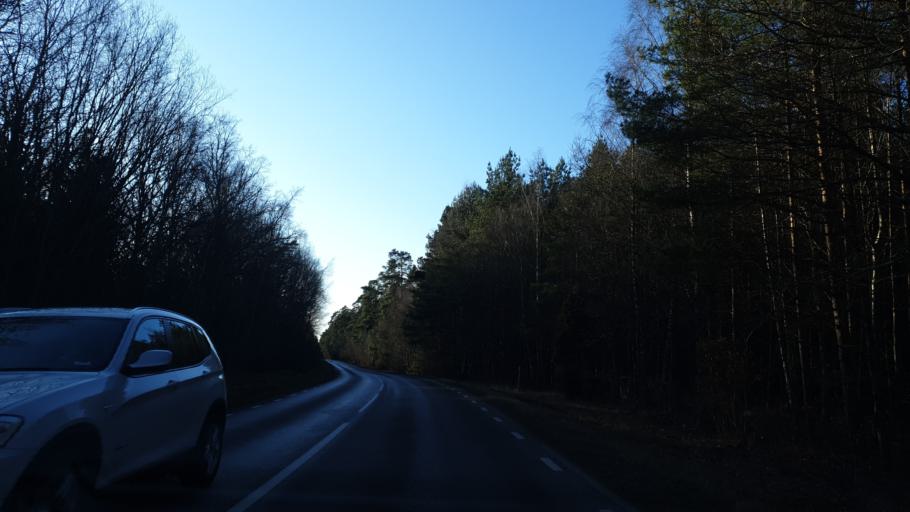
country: SE
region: Blekinge
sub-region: Ronneby Kommun
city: Kallinge
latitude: 56.2155
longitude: 15.3939
